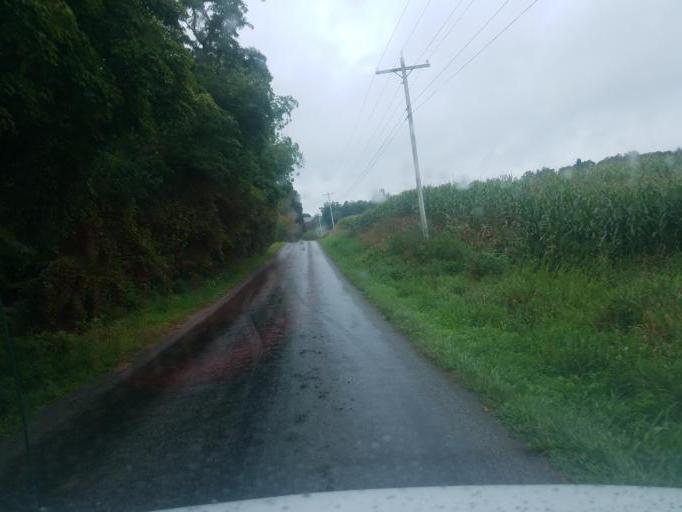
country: US
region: Ohio
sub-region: Wayne County
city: West Salem
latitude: 40.9255
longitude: -82.1378
